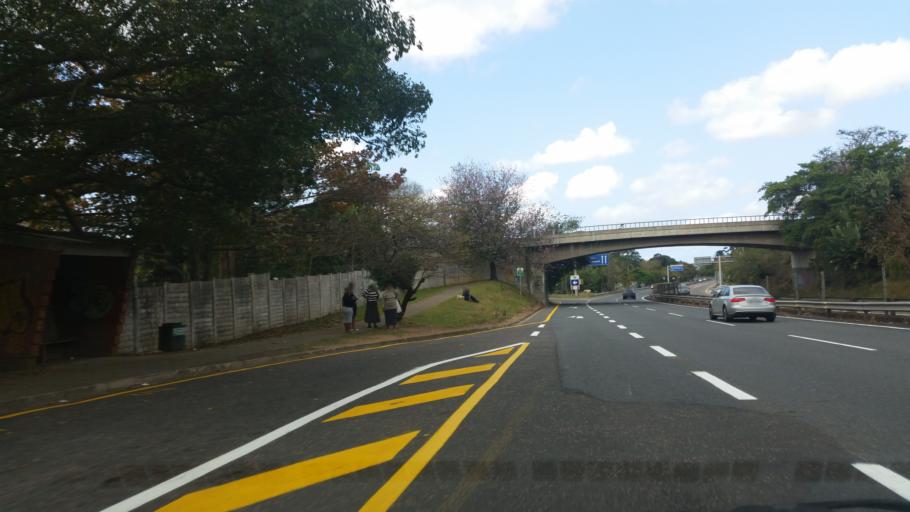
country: ZA
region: KwaZulu-Natal
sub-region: eThekwini Metropolitan Municipality
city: Berea
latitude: -29.8323
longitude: 30.9308
